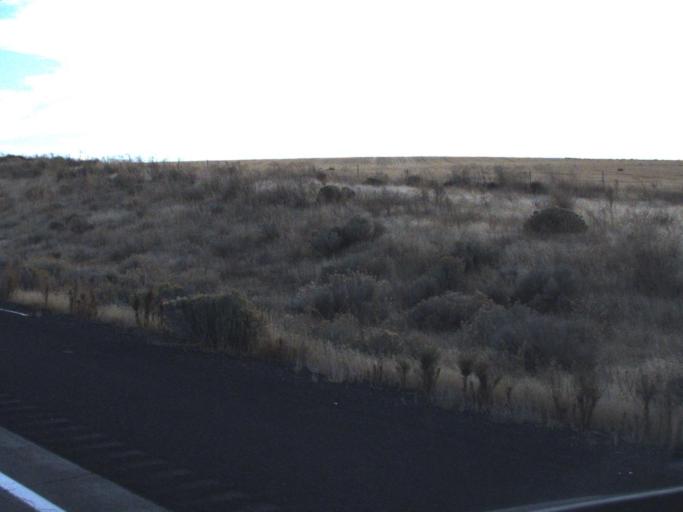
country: US
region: Washington
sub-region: Franklin County
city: Connell
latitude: 46.8039
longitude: -118.7272
